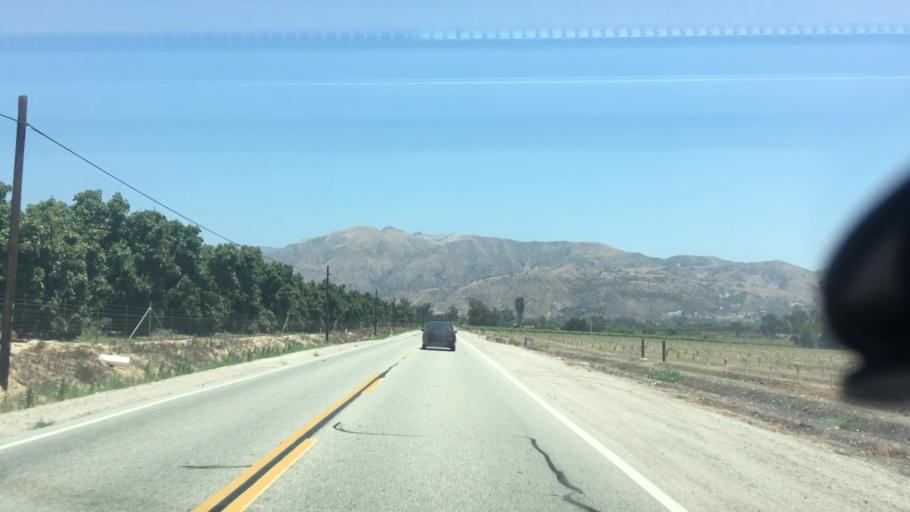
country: US
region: California
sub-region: Ventura County
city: Fillmore
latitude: 34.3946
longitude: -118.9541
